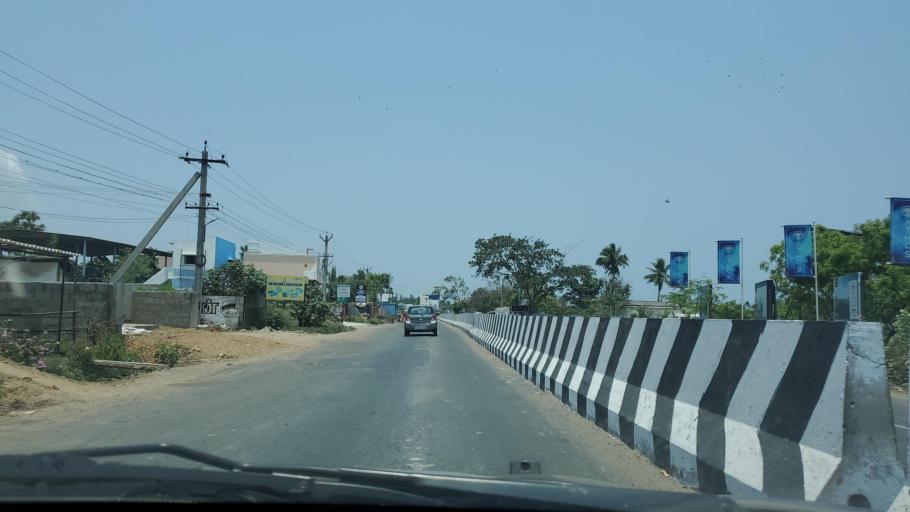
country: IN
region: Tamil Nadu
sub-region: Kancheepuram
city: Vengavasal
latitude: 12.8604
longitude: 80.1732
